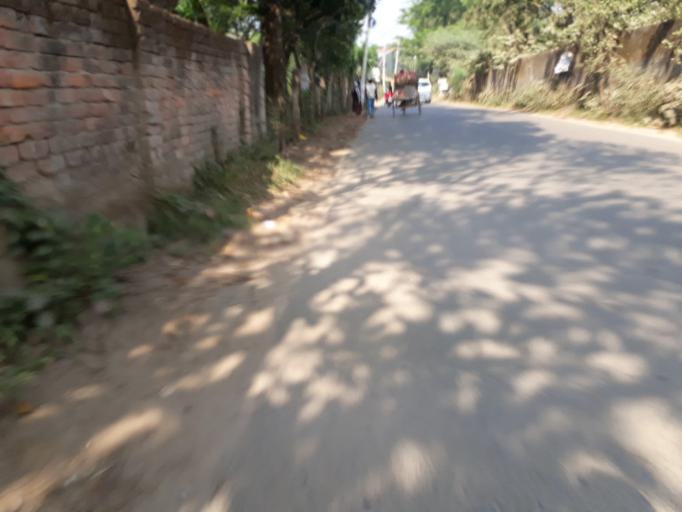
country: BD
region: Dhaka
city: Tungi
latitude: 23.8691
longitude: 90.3099
